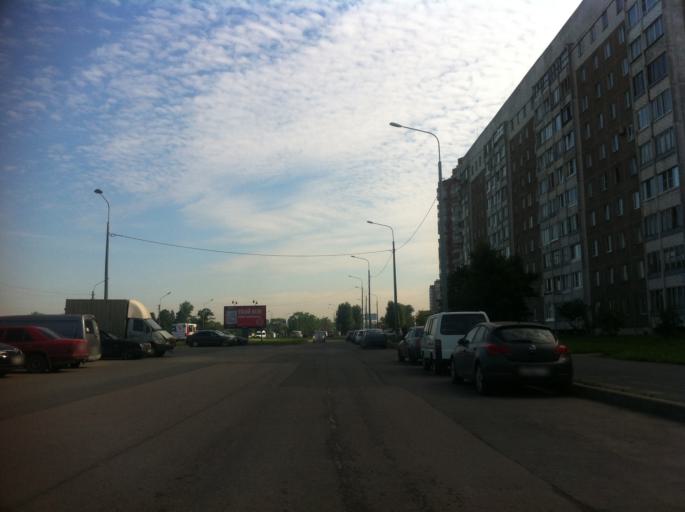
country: RU
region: St.-Petersburg
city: Uritsk
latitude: 59.8301
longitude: 30.1917
